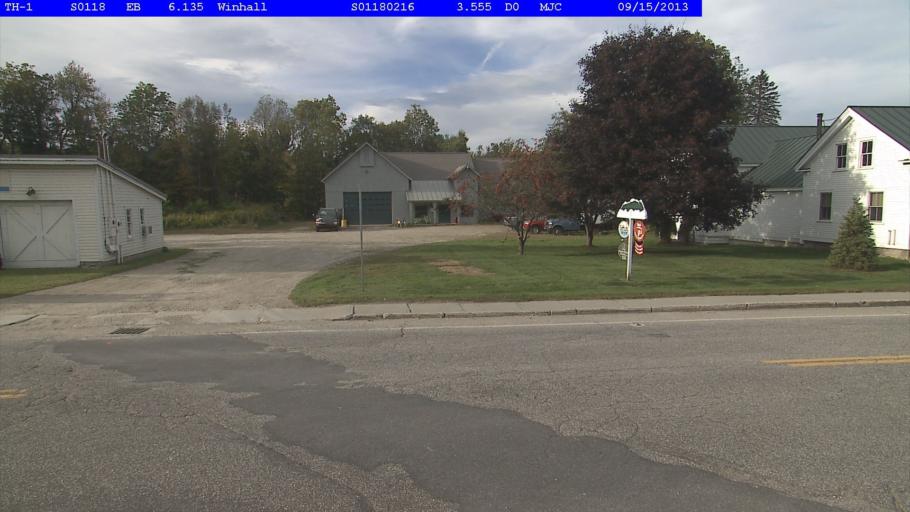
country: US
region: Vermont
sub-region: Bennington County
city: Manchester Center
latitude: 43.1446
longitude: -72.8737
